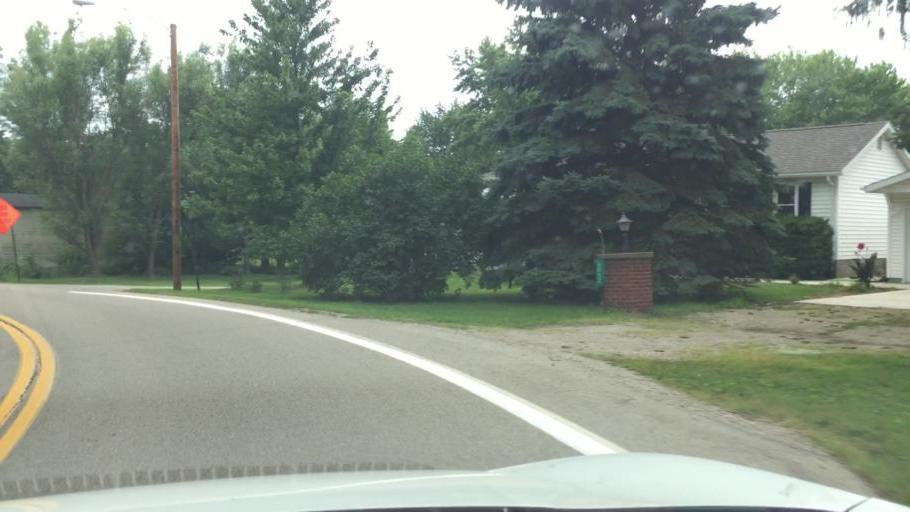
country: US
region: Ohio
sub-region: Champaign County
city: Mechanicsburg
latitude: 40.0800
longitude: -83.6365
